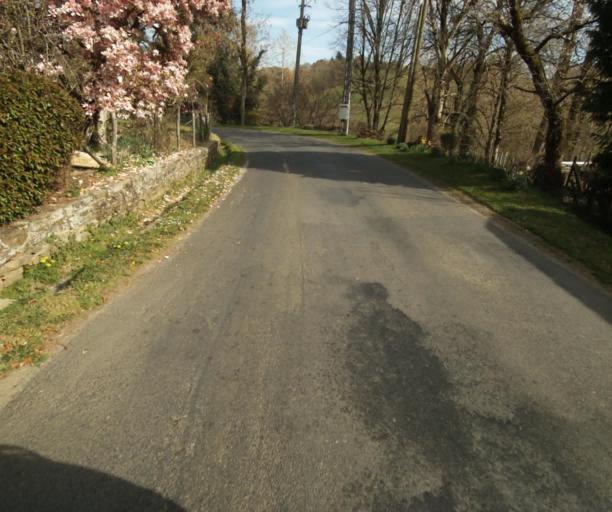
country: FR
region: Limousin
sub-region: Departement de la Correze
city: Naves
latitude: 45.3286
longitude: 1.7348
